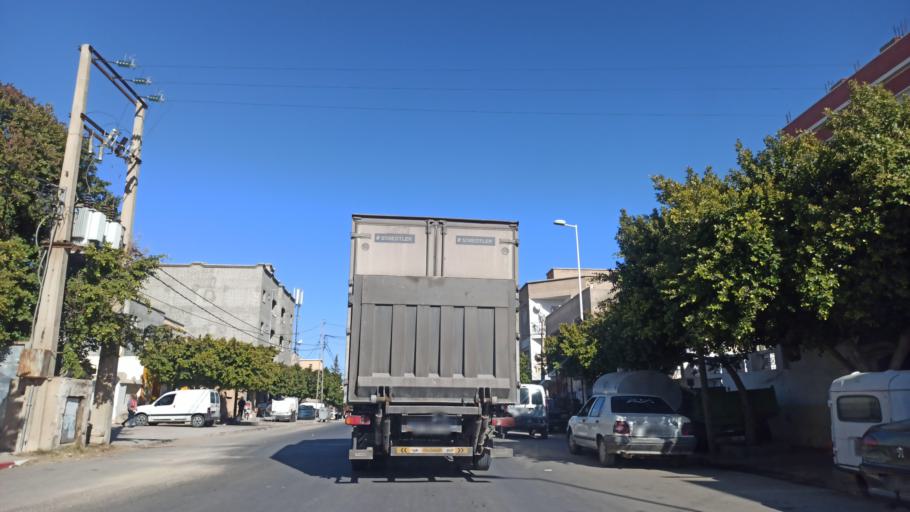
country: TN
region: Sidi Bu Zayd
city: Bi'r al Hufayy
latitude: 34.9346
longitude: 9.1980
